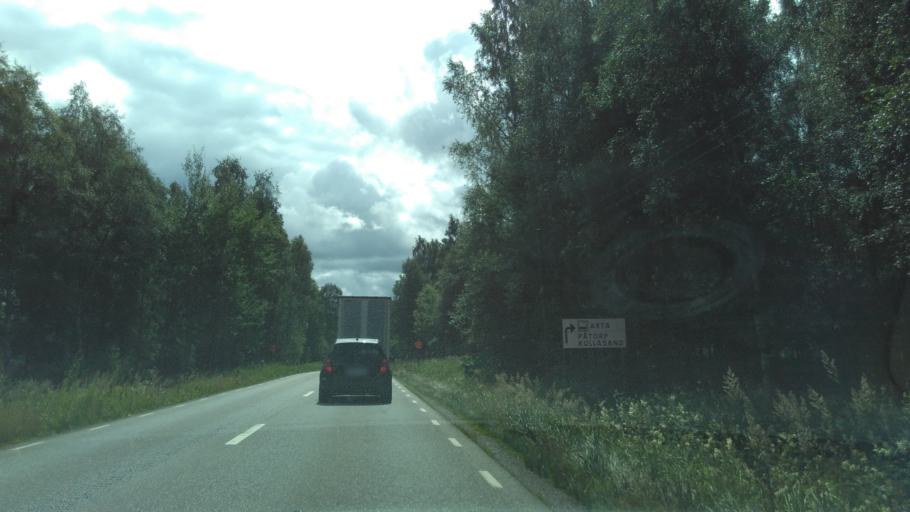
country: SE
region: Vaestra Goetaland
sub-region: Boras Kommun
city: Boras
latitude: 57.8313
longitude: 12.9942
